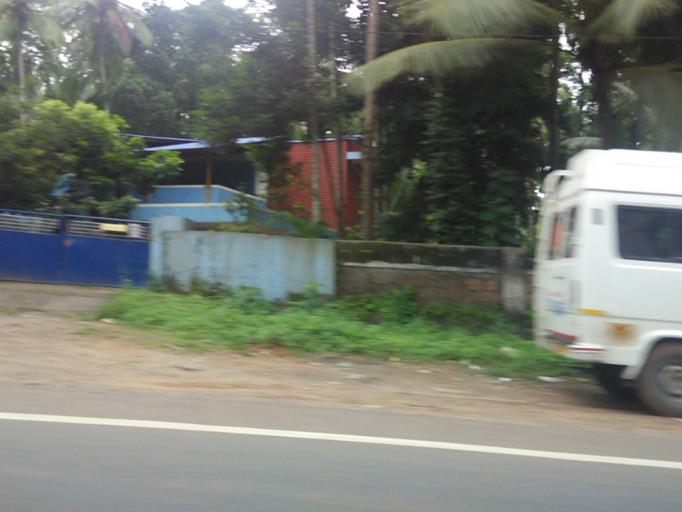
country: IN
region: Kerala
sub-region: Kozhikode
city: Kunnamangalam
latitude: 11.2976
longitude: 75.8495
